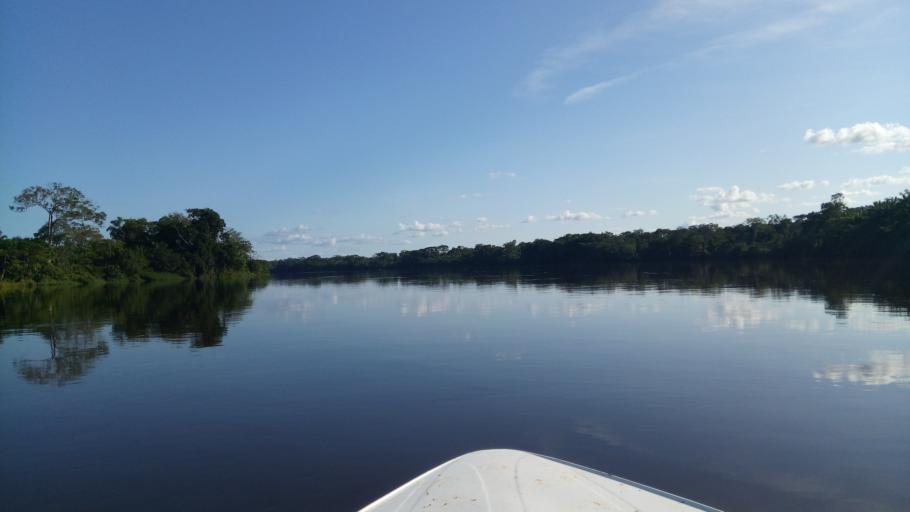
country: CD
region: Eastern Province
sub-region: Sous-Region de la Tshopo
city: Yangambi
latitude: 0.3401
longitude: 24.1316
